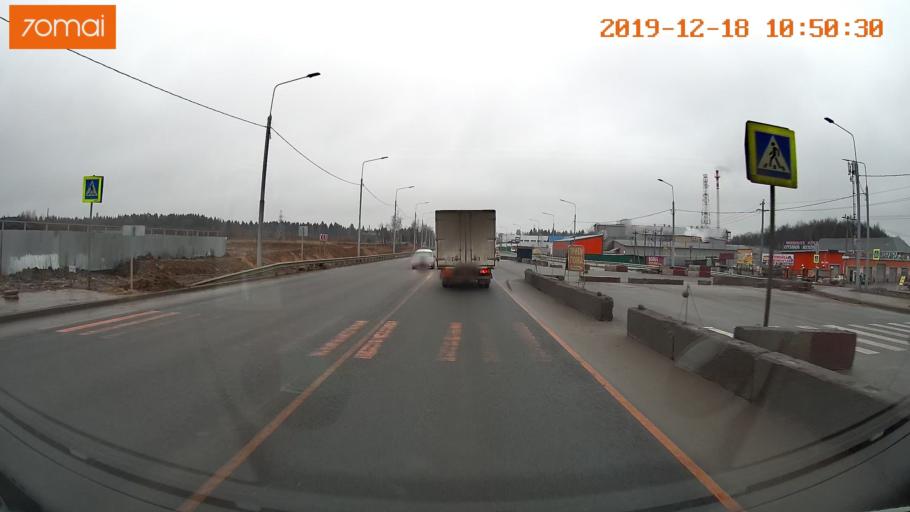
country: RU
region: Moskovskaya
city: Selyatino
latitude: 55.5094
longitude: 37.0065
